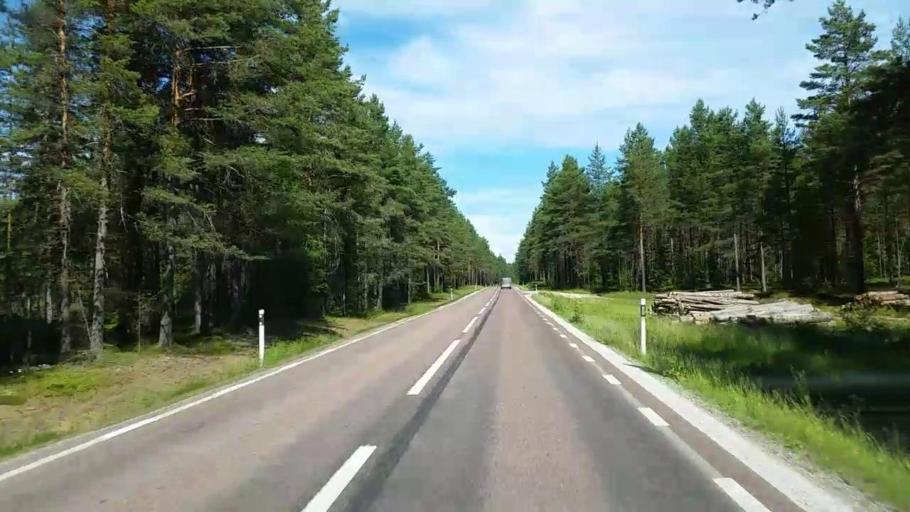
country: SE
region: Dalarna
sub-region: Rattviks Kommun
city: Raettvik
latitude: 60.9123
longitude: 15.2011
